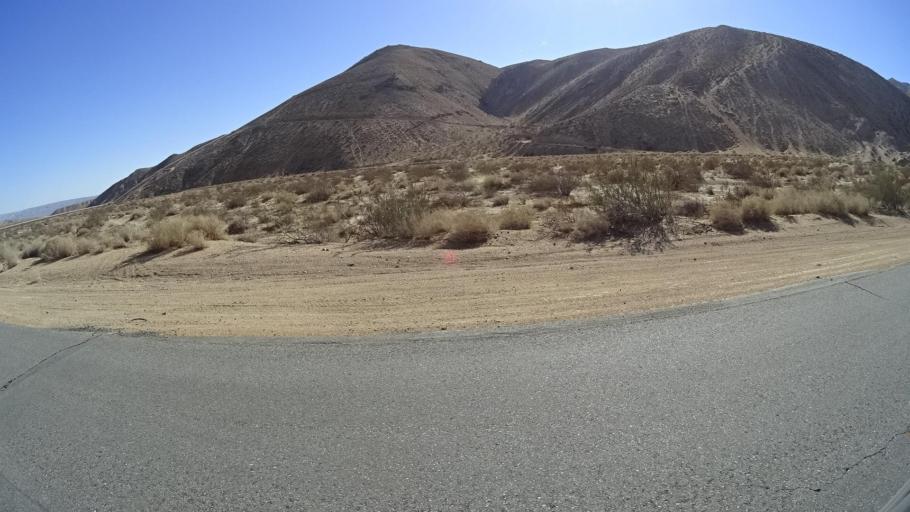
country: US
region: California
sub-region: Kern County
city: California City
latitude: 35.3164
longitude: -118.0505
